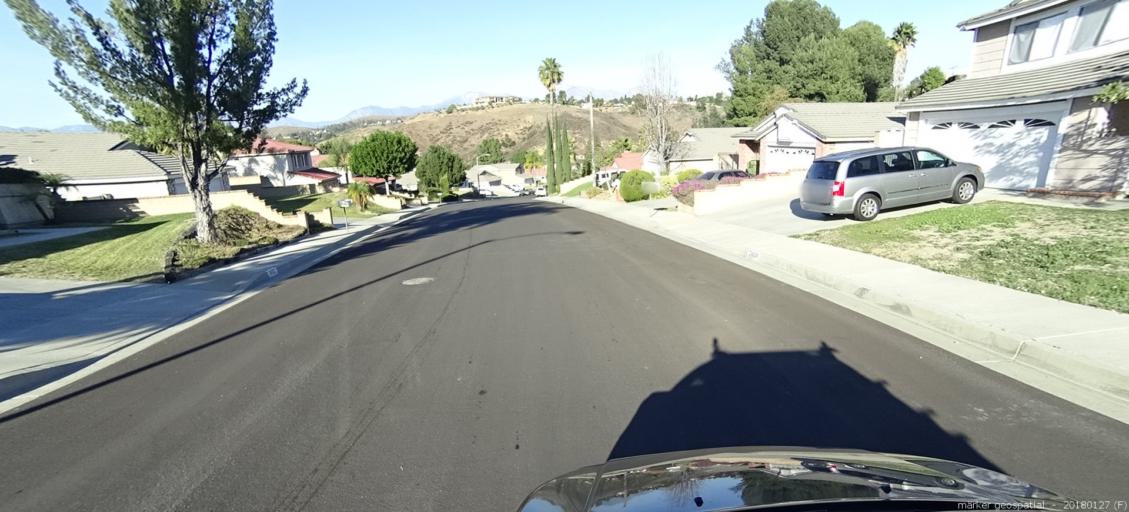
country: US
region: California
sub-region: Los Angeles County
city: Diamond Bar
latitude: 34.0231
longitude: -117.7934
